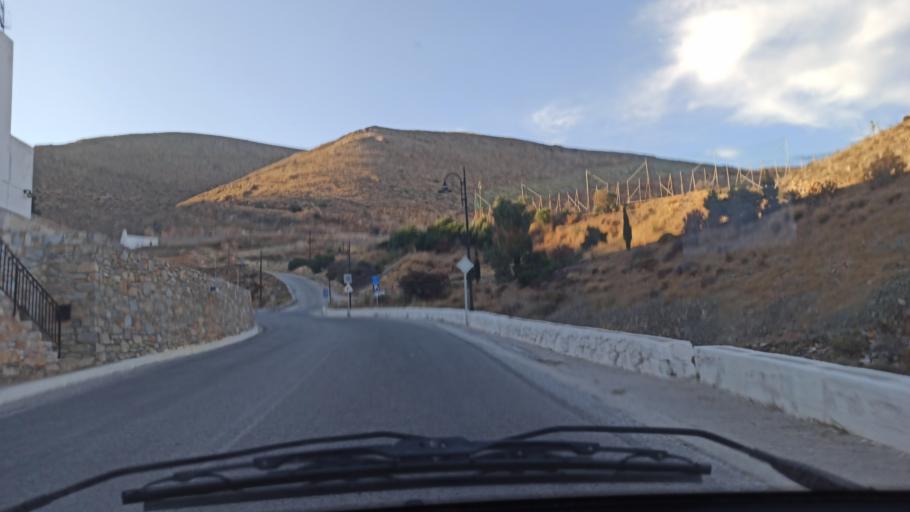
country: GR
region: South Aegean
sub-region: Nomos Kykladon
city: Ano Syros
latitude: 37.4520
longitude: 24.9368
